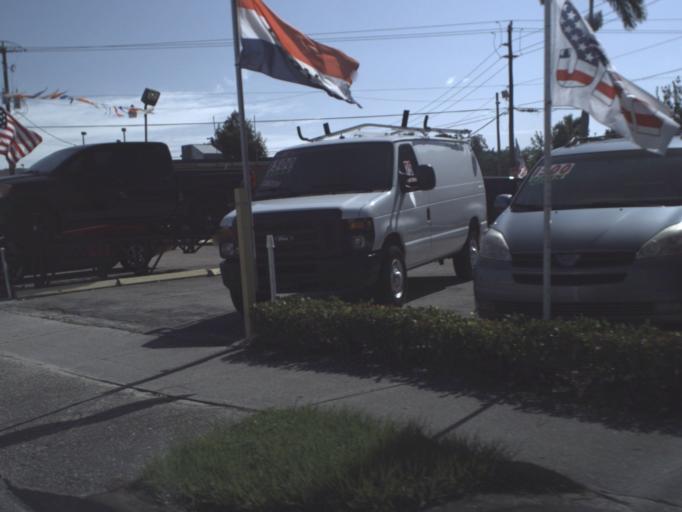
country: US
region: Florida
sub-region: Lee County
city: Tice
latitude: 26.6669
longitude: -81.8293
